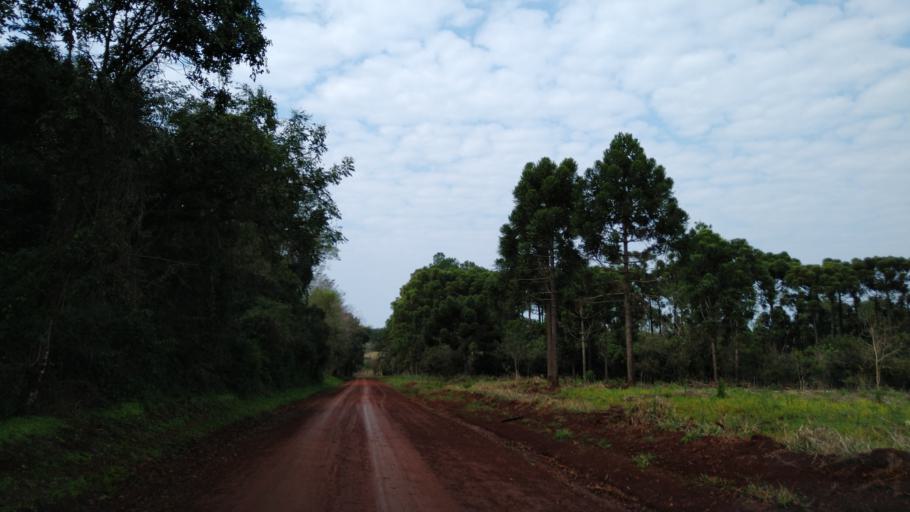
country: AR
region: Misiones
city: Ruiz de Montoya
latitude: -26.9596
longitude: -55.0588
